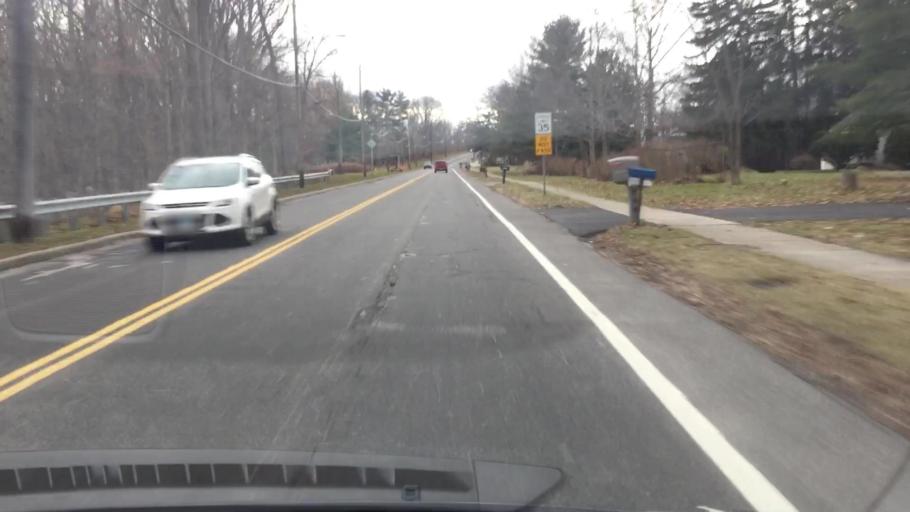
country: US
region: Ohio
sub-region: Cuyahoga County
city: Brecksville
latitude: 41.3245
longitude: -81.6124
